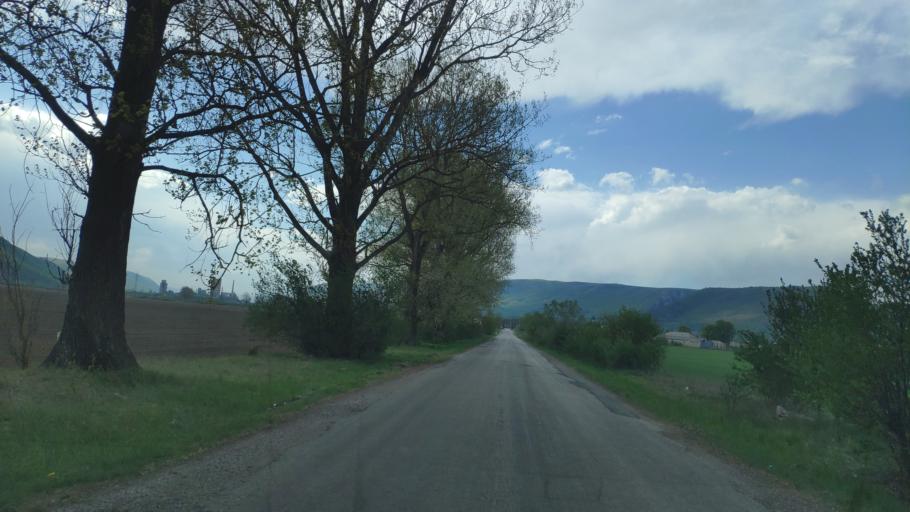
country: SK
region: Kosicky
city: Medzev
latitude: 48.5941
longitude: 20.8923
